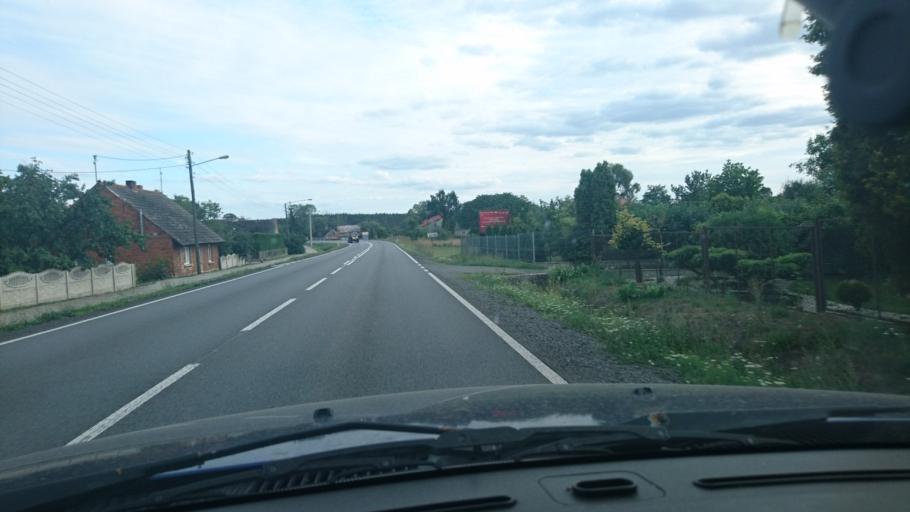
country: PL
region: Greater Poland Voivodeship
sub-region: Powiat ostrzeszowski
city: Ostrzeszow
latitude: 51.3523
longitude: 17.9475
